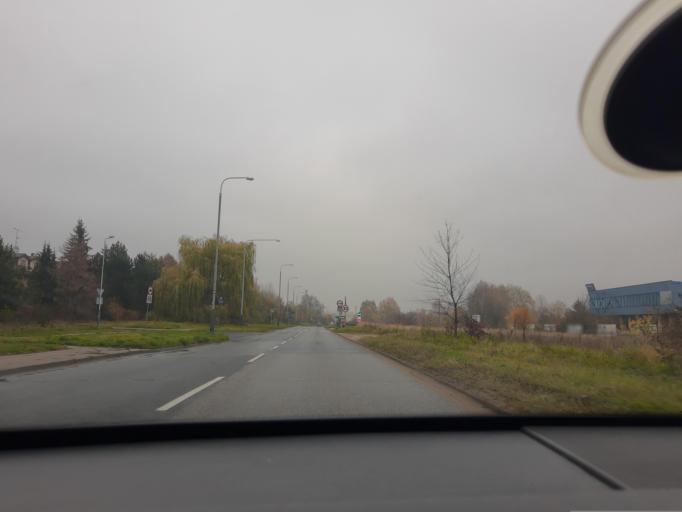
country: PL
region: Lodz Voivodeship
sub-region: Powiat pabianicki
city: Konstantynow Lodzki
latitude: 51.7348
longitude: 19.3756
